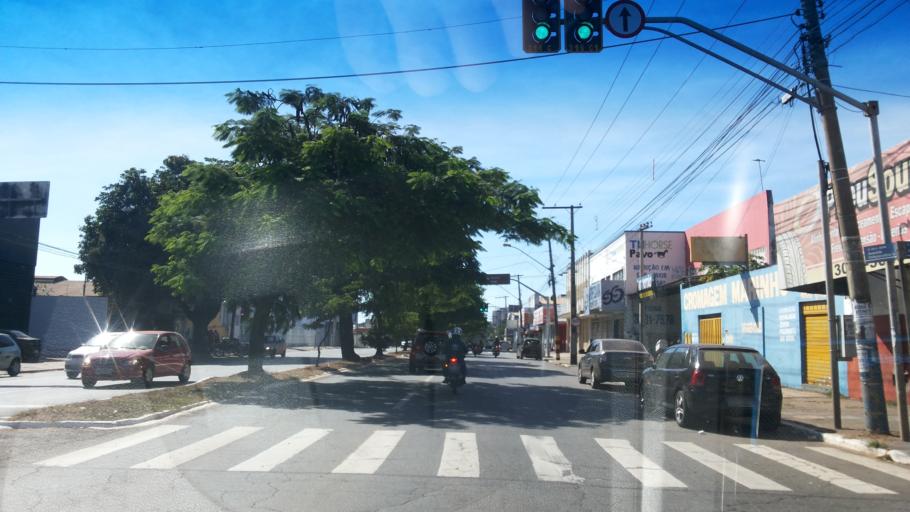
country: BR
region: Goias
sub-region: Goiania
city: Goiania
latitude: -16.6610
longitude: -49.2501
